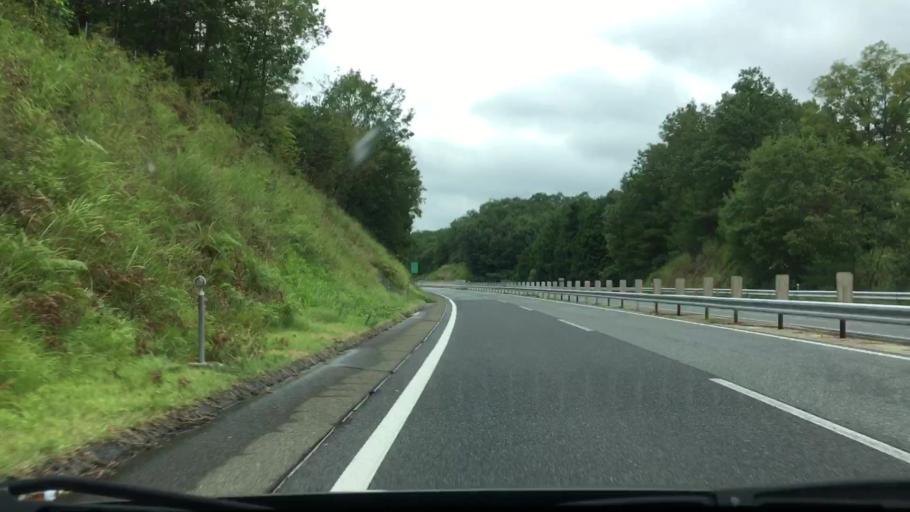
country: JP
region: Hiroshima
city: Shobara
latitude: 34.8393
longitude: 133.0431
